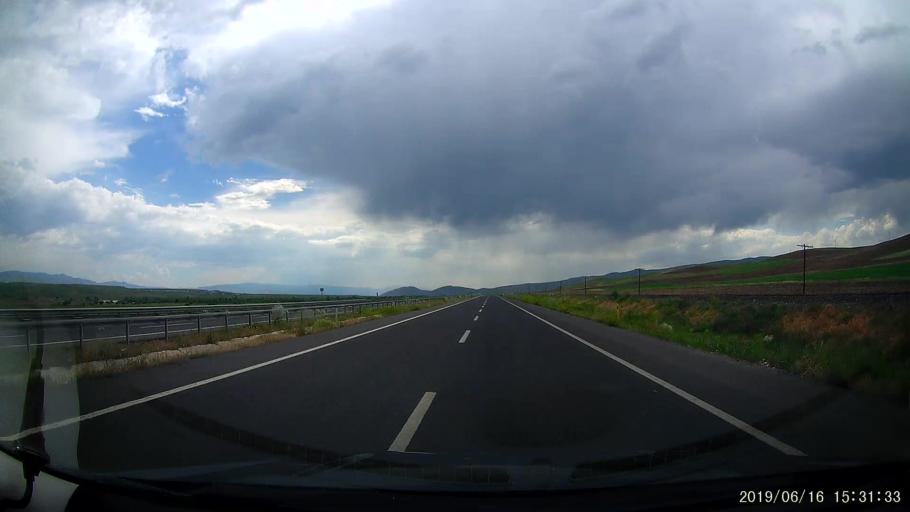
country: TR
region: Erzurum
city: Horasan
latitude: 40.0319
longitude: 42.0752
